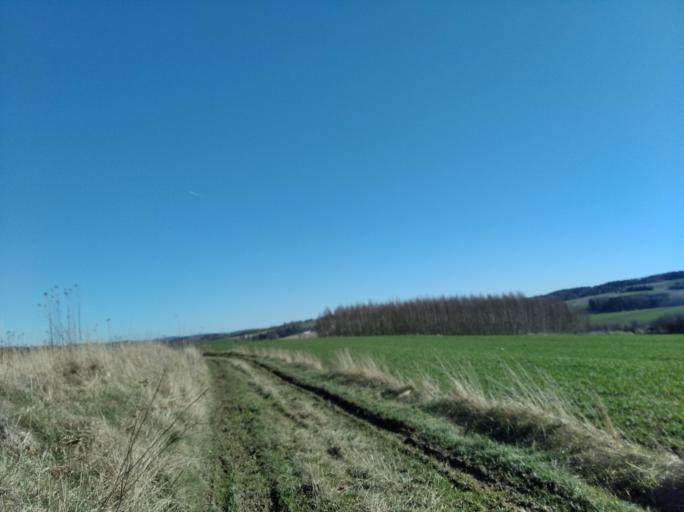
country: PL
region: Subcarpathian Voivodeship
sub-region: Powiat strzyzowski
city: Wisniowa
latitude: 49.9145
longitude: 21.6835
